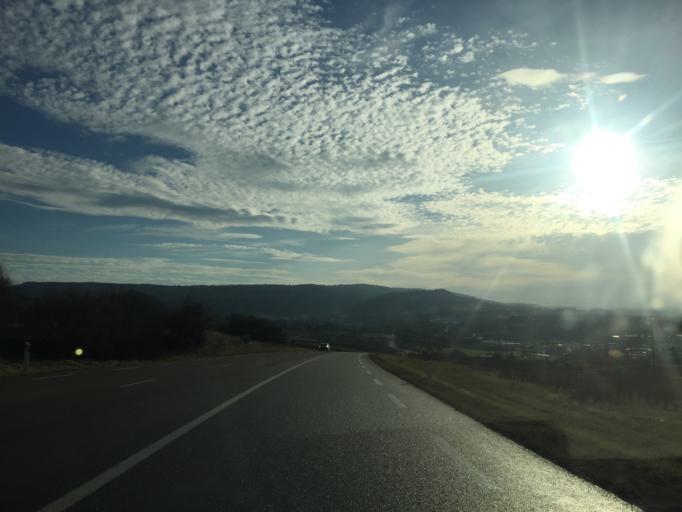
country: FR
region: Franche-Comte
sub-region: Departement du Jura
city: Arbois
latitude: 46.9281
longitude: 5.7756
